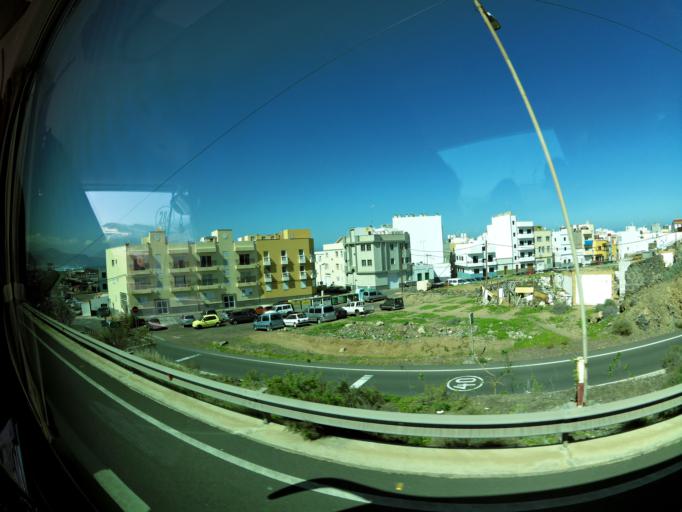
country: ES
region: Canary Islands
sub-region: Provincia de Las Palmas
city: Arucas
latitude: 28.1496
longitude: -15.5333
